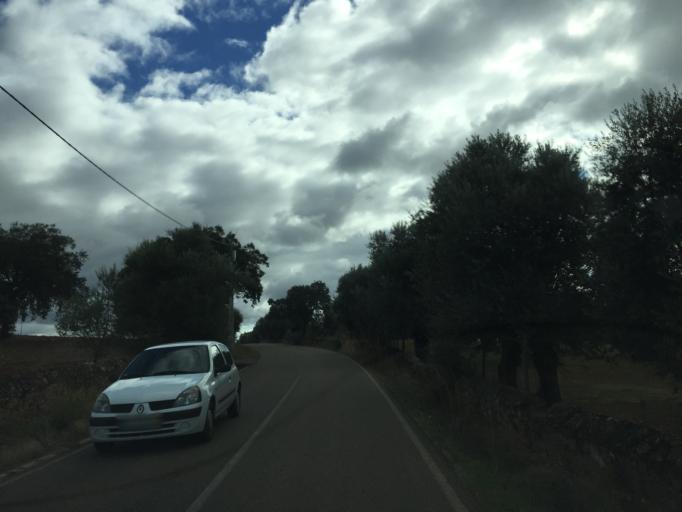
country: PT
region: Portalegre
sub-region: Alter do Chao
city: Alter do Chao
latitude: 39.2125
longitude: -7.6673
